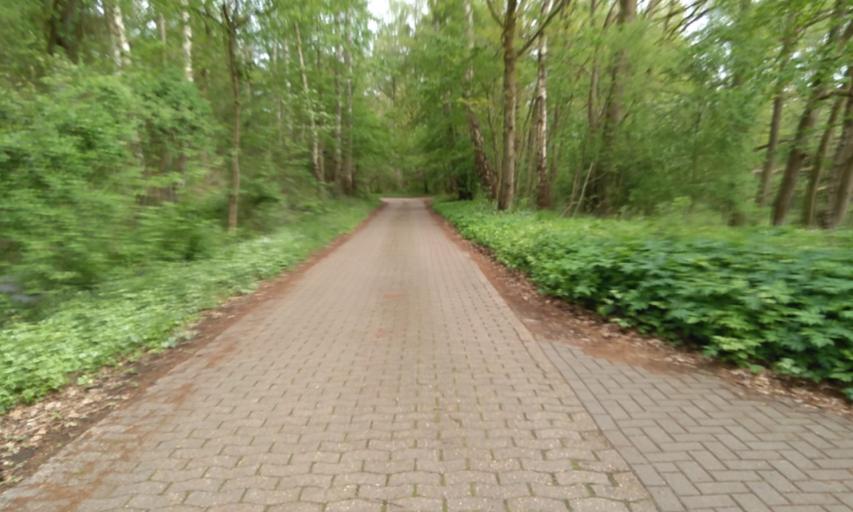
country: DE
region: Lower Saxony
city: Buxtehude
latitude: 53.4394
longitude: 9.6574
